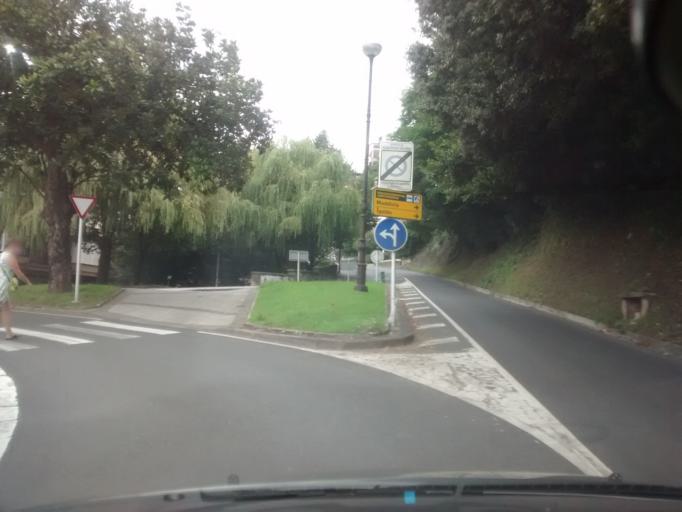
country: ES
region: Basque Country
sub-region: Provincia de Guipuzcoa
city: San Sebastian
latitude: 43.3153
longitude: -2.0068
